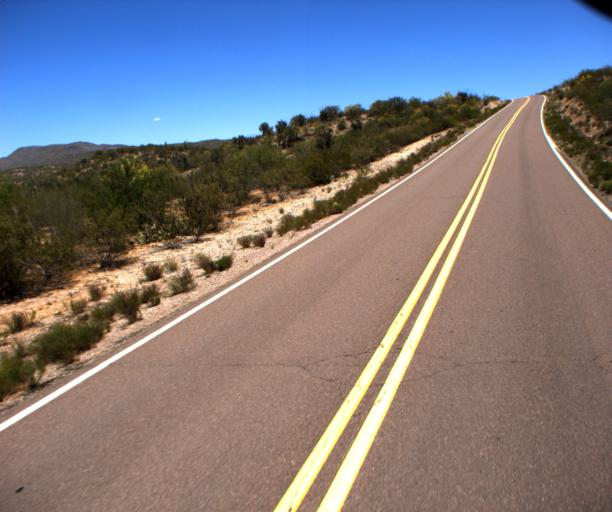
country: US
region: Arizona
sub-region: Yavapai County
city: Bagdad
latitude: 34.4720
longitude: -113.2132
